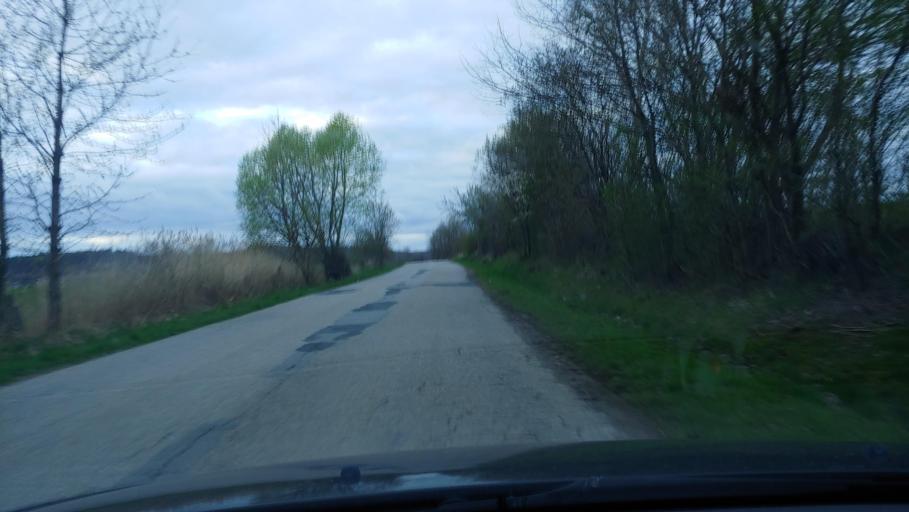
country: PL
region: Lesser Poland Voivodeship
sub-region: Powiat krakowski
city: Rudawa
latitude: 50.1401
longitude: 19.7506
